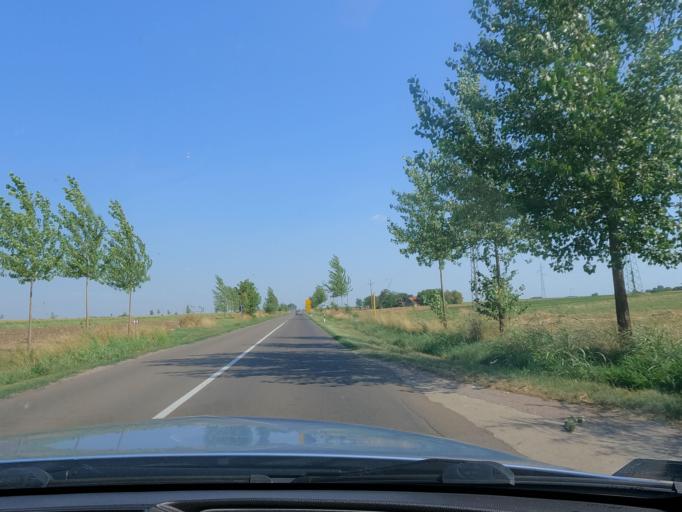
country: RS
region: Autonomna Pokrajina Vojvodina
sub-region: Severnobacki Okrug
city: Backa Topola
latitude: 45.8018
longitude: 19.6555
